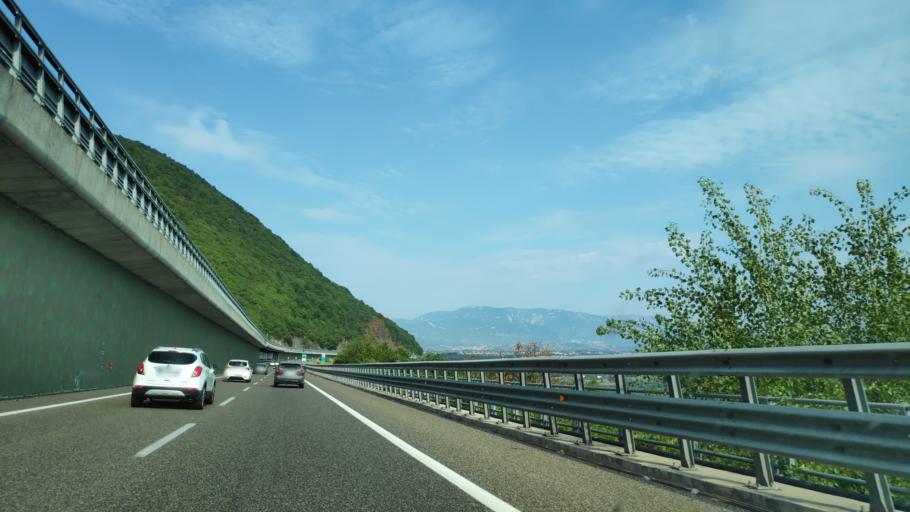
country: IT
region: Campania
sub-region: Provincia di Salerno
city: Sicignano degli Alburni
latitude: 40.5911
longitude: 15.3295
